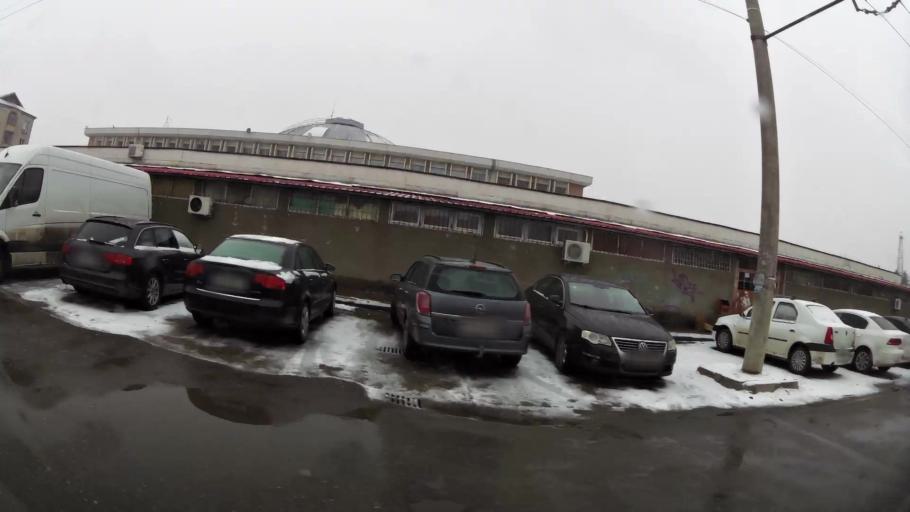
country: RO
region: Dambovita
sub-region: Municipiul Targoviste
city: Targoviste
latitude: 44.9183
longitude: 25.4508
